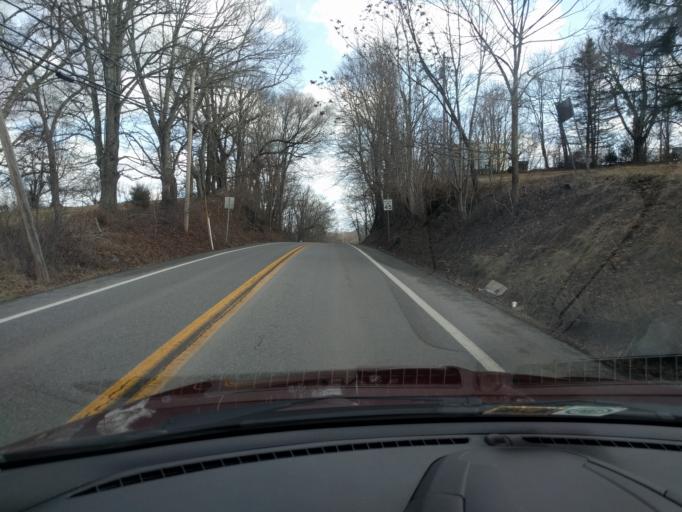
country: US
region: West Virginia
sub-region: Greenbrier County
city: Lewisburg
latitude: 37.7962
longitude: -80.4353
